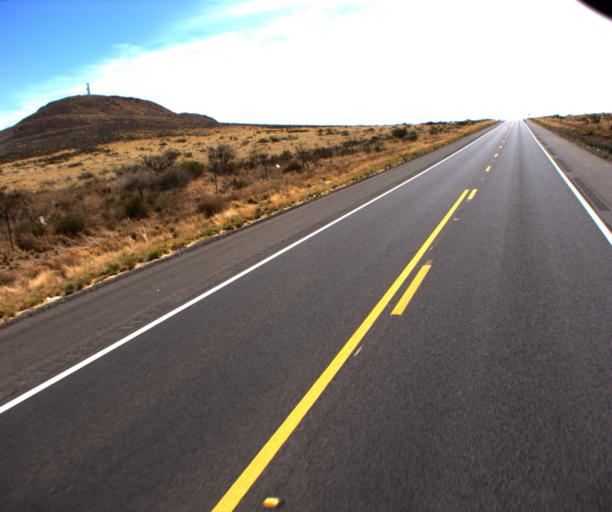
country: US
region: Arizona
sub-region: Cochise County
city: Willcox
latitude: 31.9043
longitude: -109.7174
